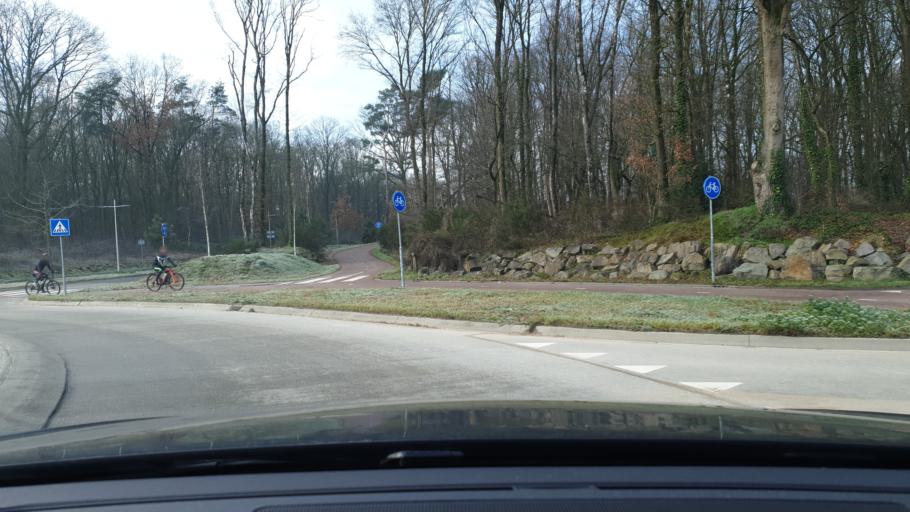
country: NL
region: North Brabant
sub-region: Gemeente Veldhoven
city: Oerle
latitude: 51.4168
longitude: 5.3680
